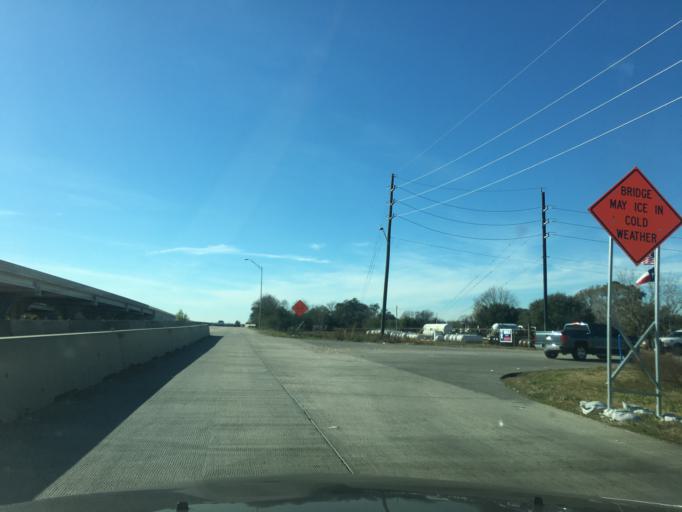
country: US
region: Texas
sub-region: Fort Bend County
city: Rosenberg
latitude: 29.5322
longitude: -95.8186
